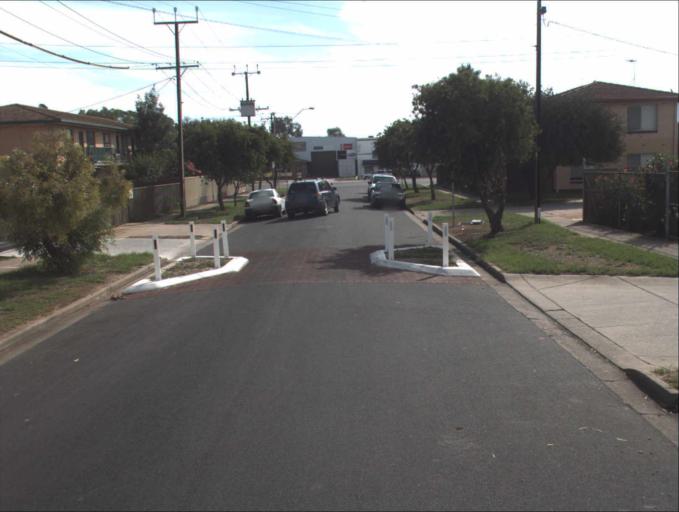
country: AU
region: South Australia
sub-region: Port Adelaide Enfield
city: Blair Athol
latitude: -34.8610
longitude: 138.5842
